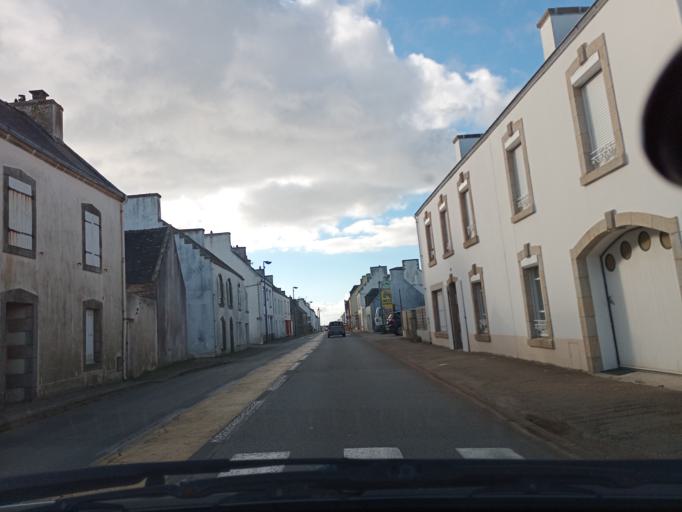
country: FR
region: Brittany
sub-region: Departement du Finistere
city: Plouhinec
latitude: 48.0147
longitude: -4.4885
